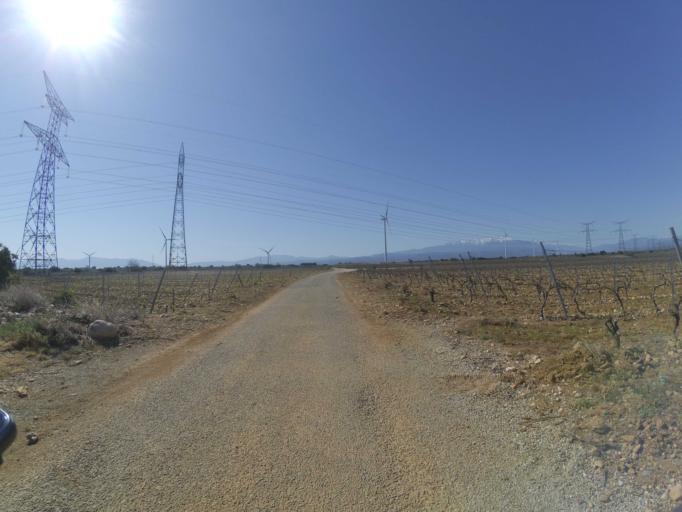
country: FR
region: Languedoc-Roussillon
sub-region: Departement des Pyrenees-Orientales
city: Pezilla-la-Riviere
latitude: 42.7249
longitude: 2.7710
